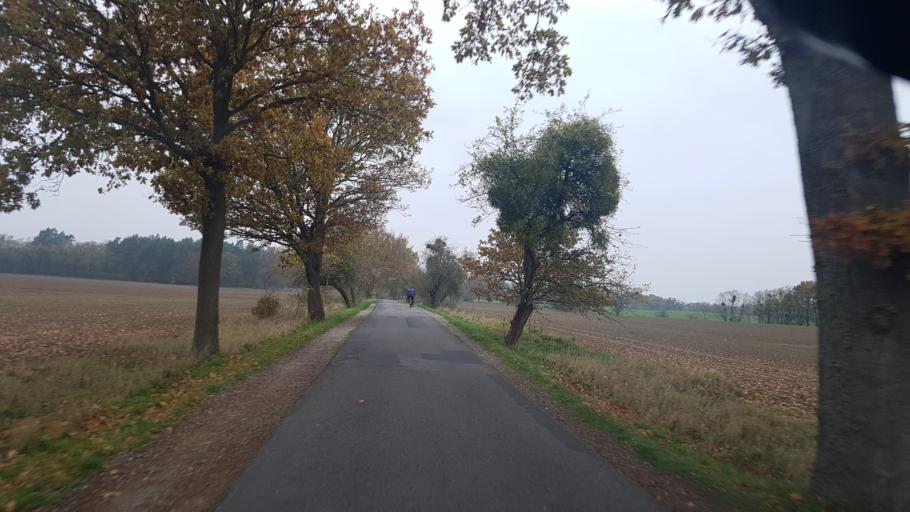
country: DE
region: Brandenburg
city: Lindow
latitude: 52.9432
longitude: 13.0558
